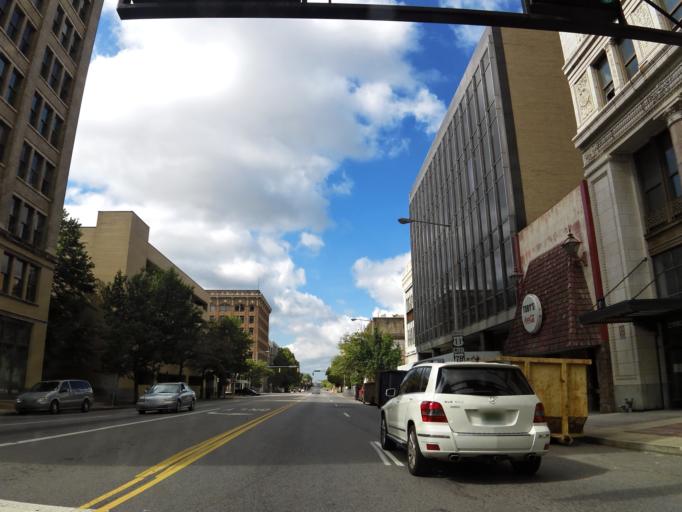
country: US
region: Alabama
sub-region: Jefferson County
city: Birmingham
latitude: 33.5144
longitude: -86.8058
